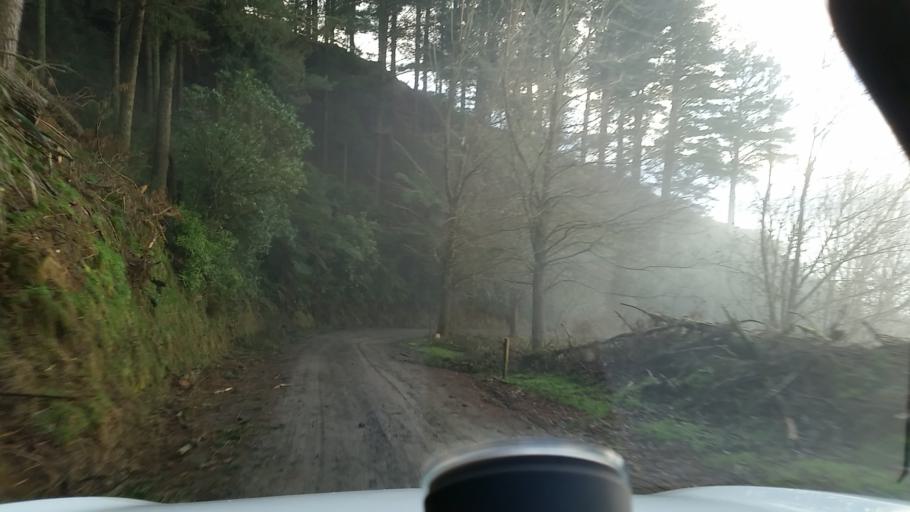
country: NZ
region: Taranaki
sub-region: South Taranaki District
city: Eltham
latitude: -39.4490
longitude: 174.4583
